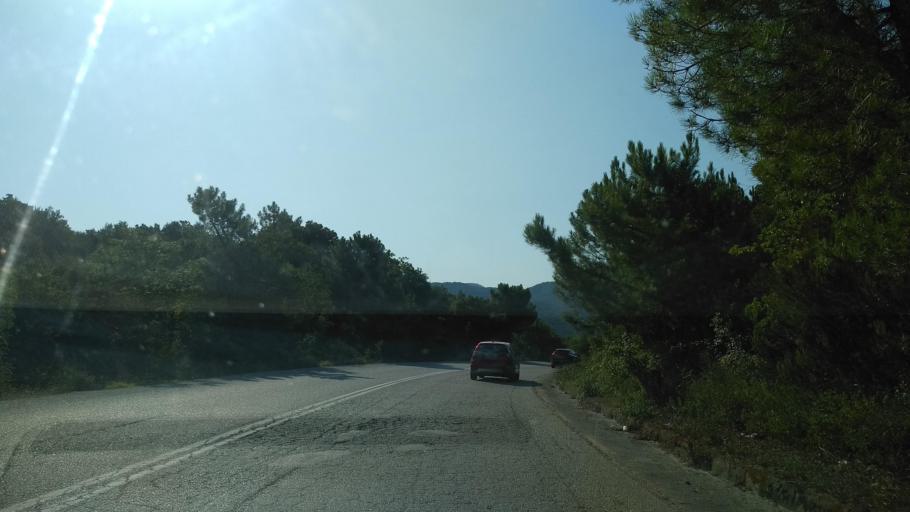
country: GR
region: Central Macedonia
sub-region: Nomos Chalkidikis
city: Stratonion
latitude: 40.5611
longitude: 23.8227
